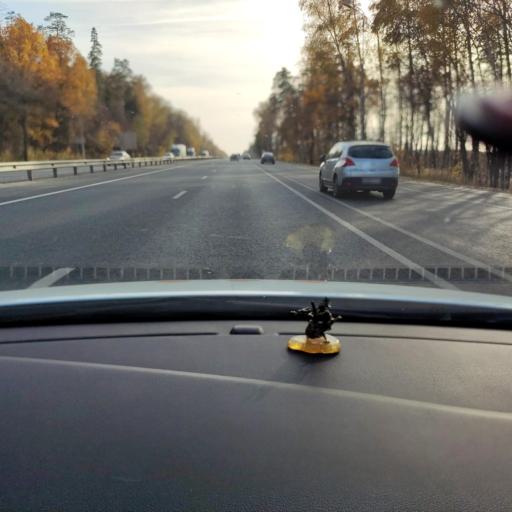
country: RU
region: Tatarstan
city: Osinovo
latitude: 55.8532
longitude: 48.8537
